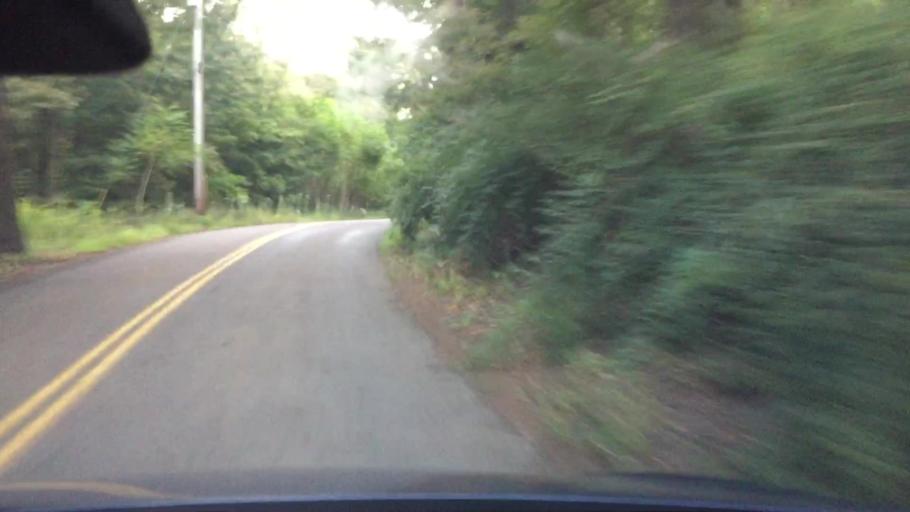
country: US
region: Pennsylvania
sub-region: Allegheny County
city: Bakerstown
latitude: 40.6273
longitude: -79.9033
